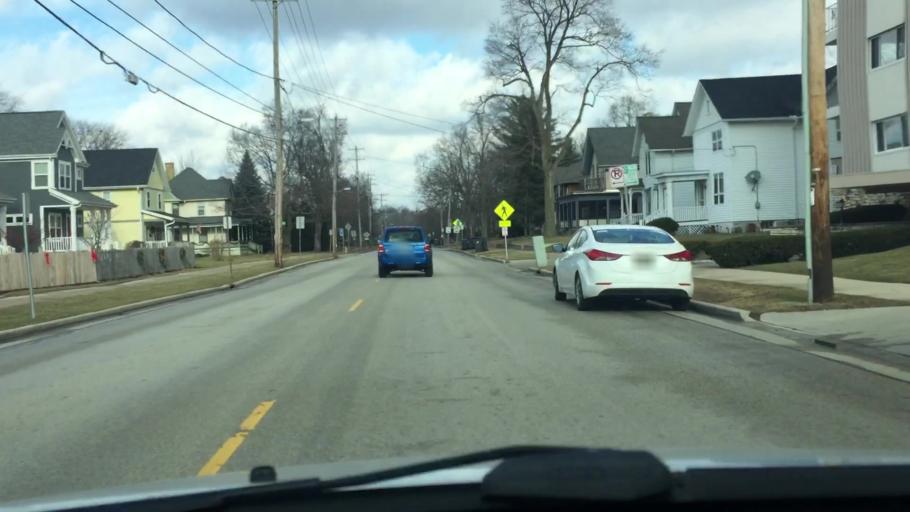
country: US
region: Wisconsin
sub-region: Waukesha County
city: Waukesha
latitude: 43.0064
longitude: -88.2366
